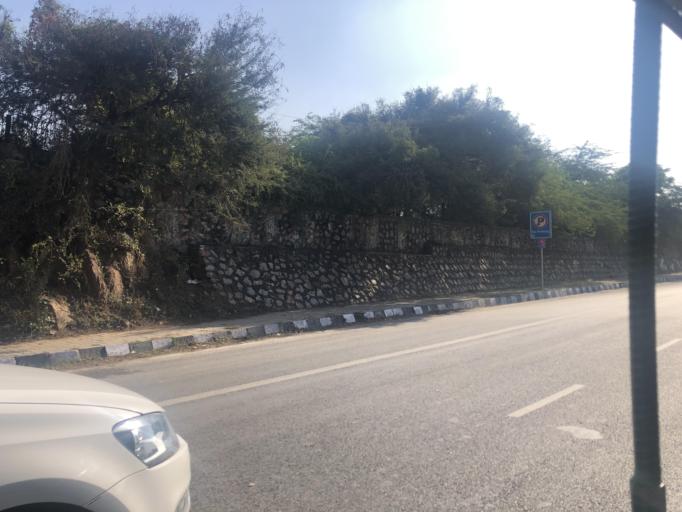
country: IN
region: NCT
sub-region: Central Delhi
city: Karol Bagh
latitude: 28.5441
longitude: 77.1594
